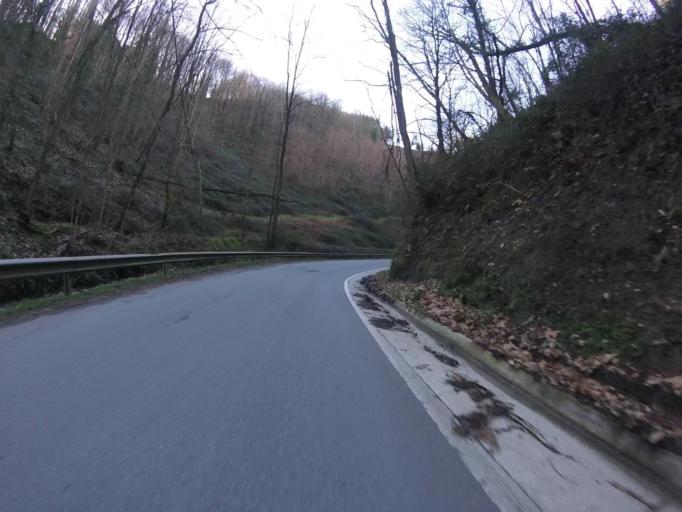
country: ES
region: Navarre
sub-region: Provincia de Navarra
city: Lesaka
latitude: 43.2487
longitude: -1.7207
